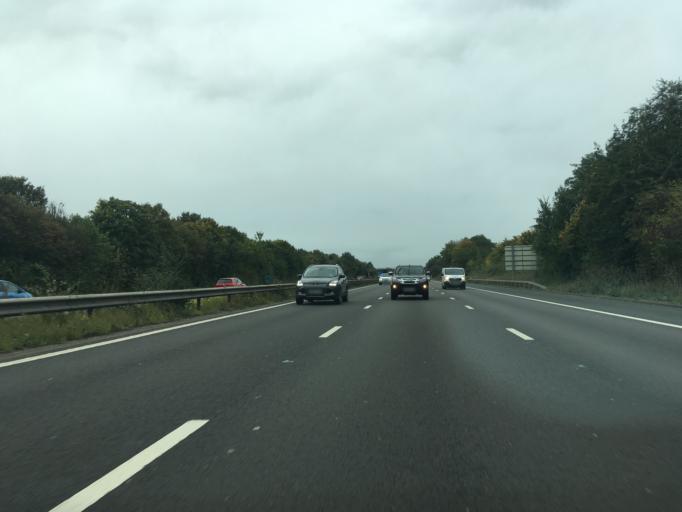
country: GB
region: England
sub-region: Worcestershire
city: Bredon
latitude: 52.0065
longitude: -2.1219
